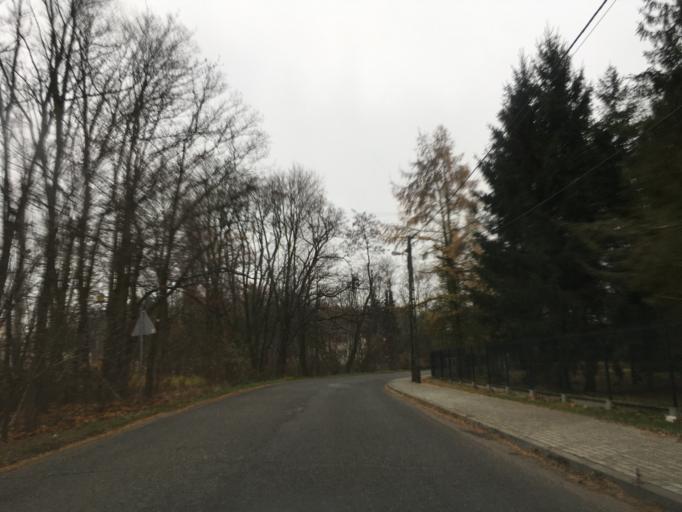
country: PL
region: Masovian Voivodeship
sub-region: Powiat piaseczynski
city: Lesznowola
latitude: 52.0735
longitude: 20.8764
